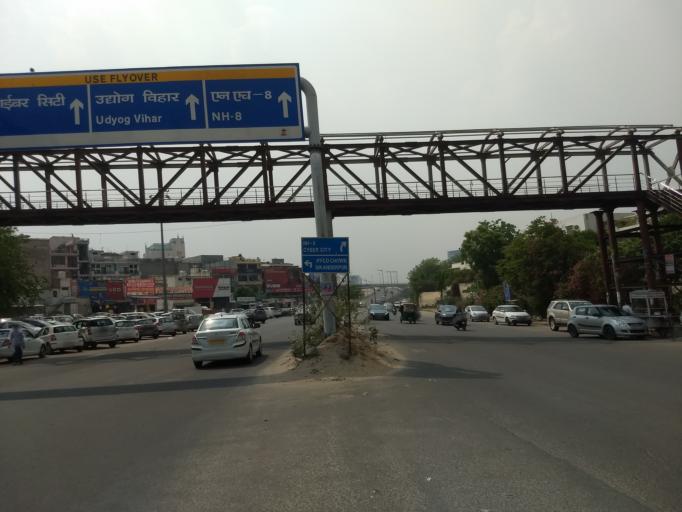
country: IN
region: Haryana
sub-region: Gurgaon
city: Gurgaon
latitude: 28.4822
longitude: 77.0998
